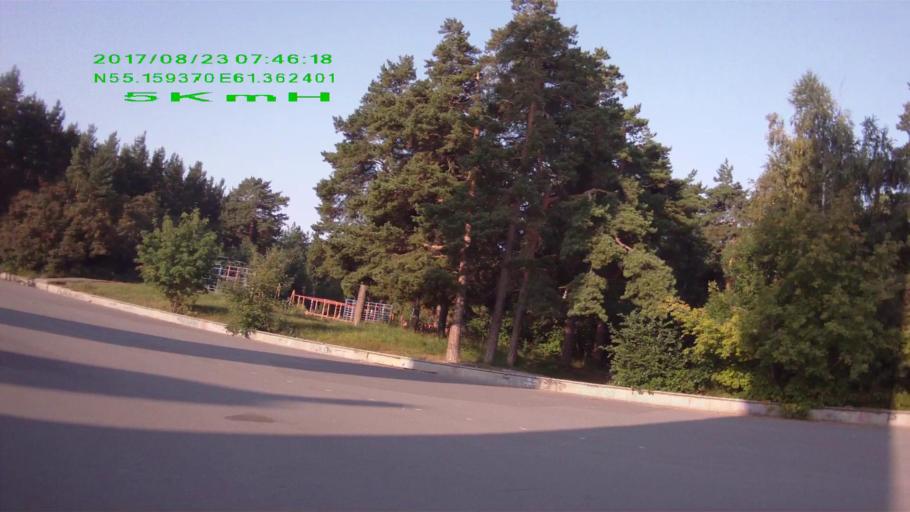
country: RU
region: Chelyabinsk
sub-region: Gorod Chelyabinsk
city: Chelyabinsk
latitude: 55.1595
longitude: 61.3637
